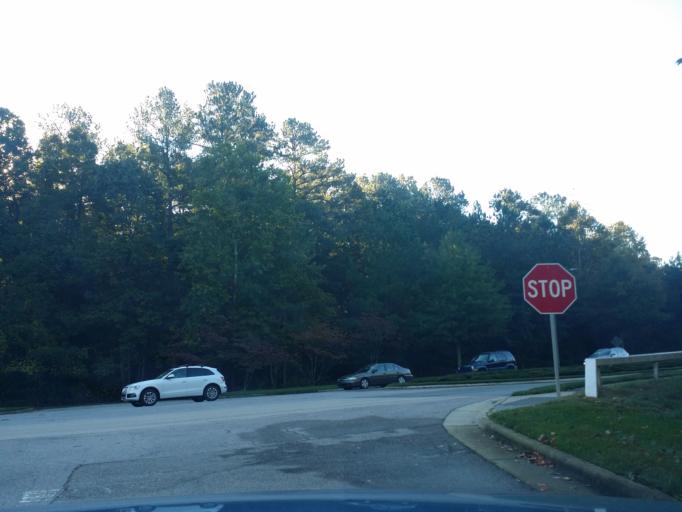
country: US
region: North Carolina
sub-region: Wake County
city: Morrisville
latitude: 35.8257
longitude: -78.8070
